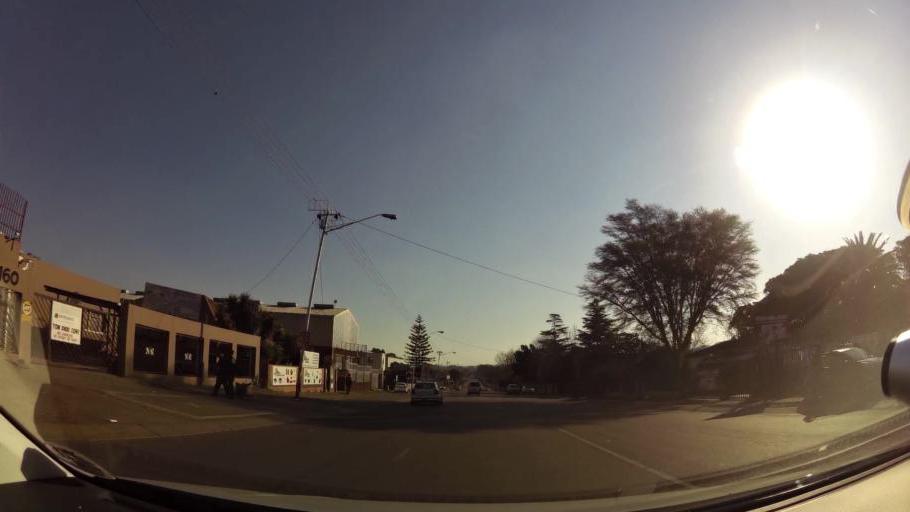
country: ZA
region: Gauteng
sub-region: City of Tshwane Metropolitan Municipality
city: Pretoria
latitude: -25.7429
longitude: 28.1690
